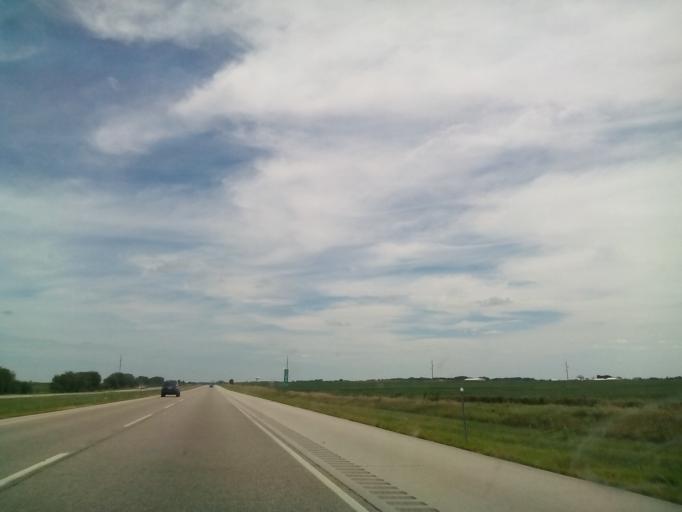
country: US
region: Illinois
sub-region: DeKalb County
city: Malta
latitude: 41.9000
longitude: -88.8168
